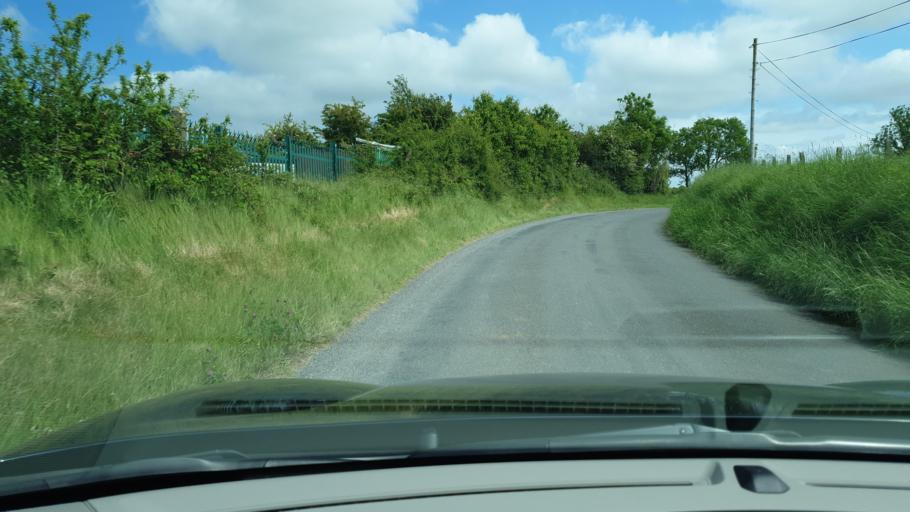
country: IE
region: Ulster
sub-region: An Cabhan
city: Kingscourt
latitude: 53.8084
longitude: -6.7325
